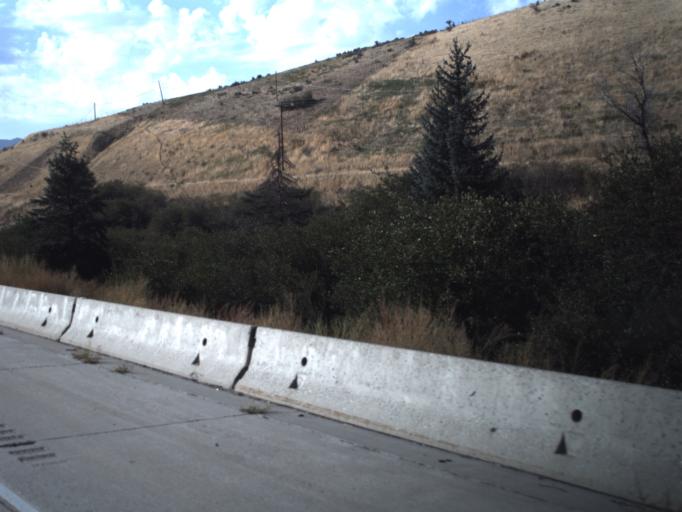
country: US
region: Utah
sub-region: Morgan County
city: Mountain Green
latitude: 41.1117
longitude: -111.7569
